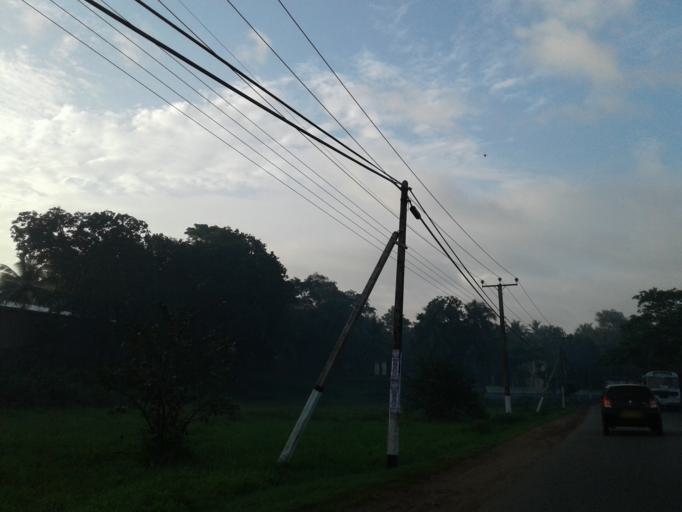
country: LK
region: Western
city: Mulleriyawa
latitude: 6.9575
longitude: 79.9947
